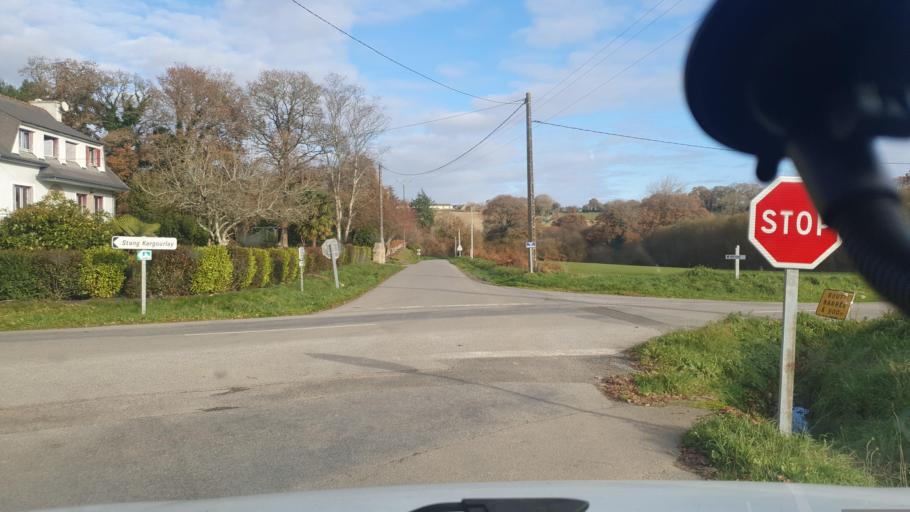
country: FR
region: Brittany
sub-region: Departement du Finistere
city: Briec
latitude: 48.1114
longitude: -3.9930
